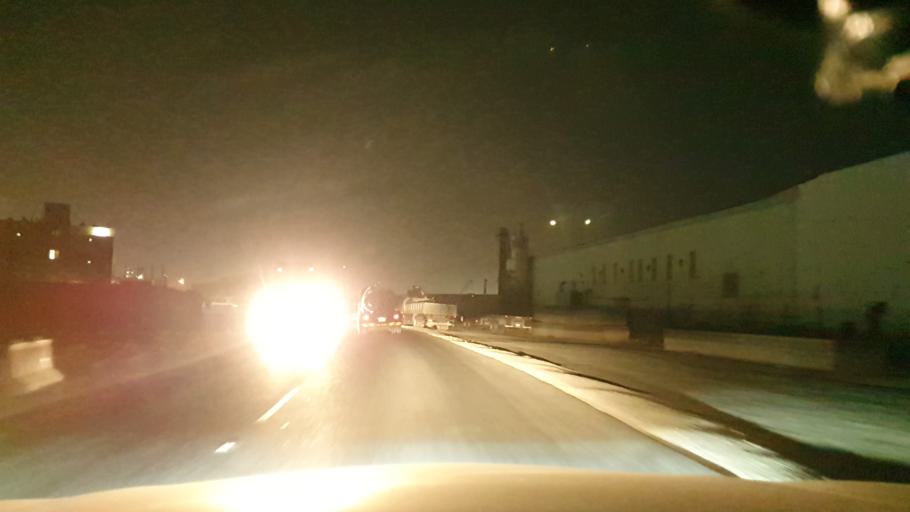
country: BH
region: Northern
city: Sitrah
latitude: 26.0958
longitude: 50.6150
